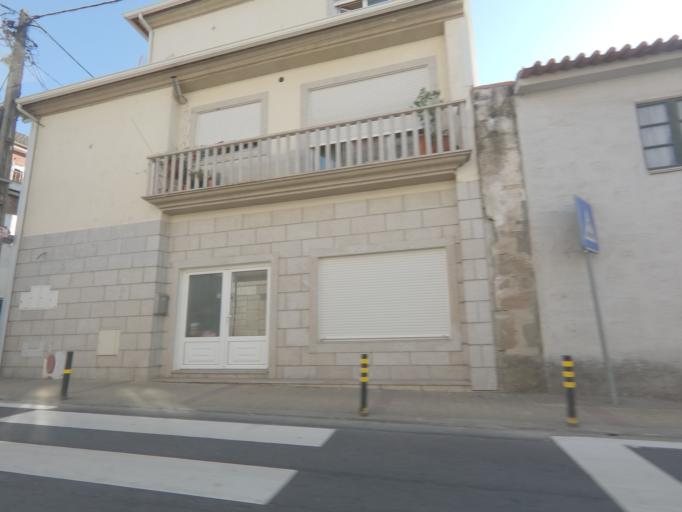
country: PT
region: Vila Real
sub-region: Vila Real
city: Vila Real
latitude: 41.2827
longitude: -7.6975
